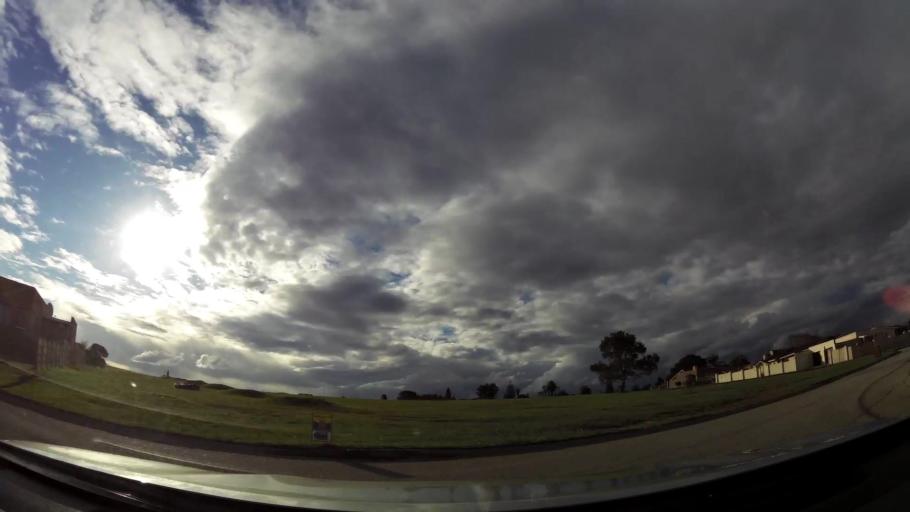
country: ZA
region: Eastern Cape
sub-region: Nelson Mandela Bay Metropolitan Municipality
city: Port Elizabeth
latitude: -33.9485
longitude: 25.4802
